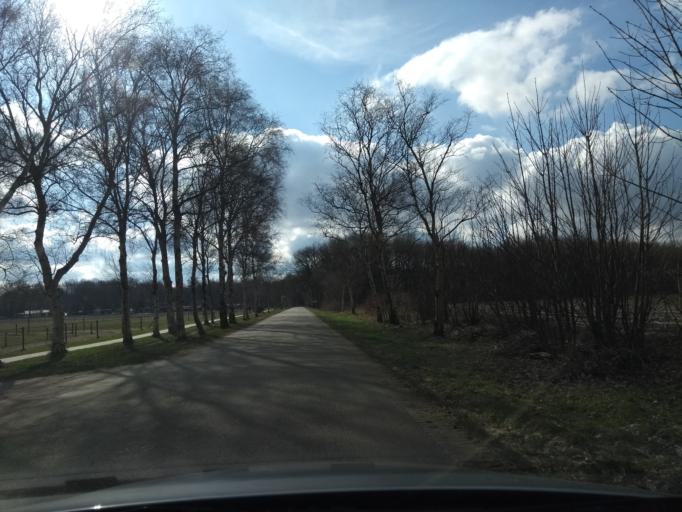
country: NL
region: Drenthe
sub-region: Gemeente Westerveld
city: Dwingeloo
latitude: 52.8245
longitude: 6.3697
